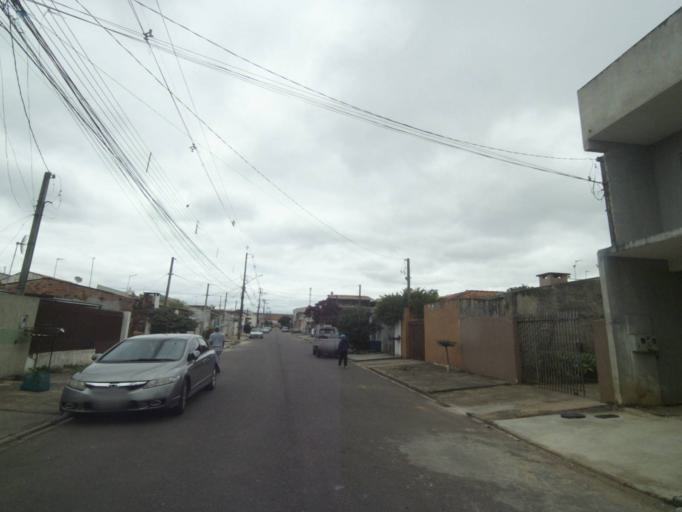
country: BR
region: Parana
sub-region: Sao Jose Dos Pinhais
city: Sao Jose dos Pinhais
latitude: -25.5550
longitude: -49.2645
